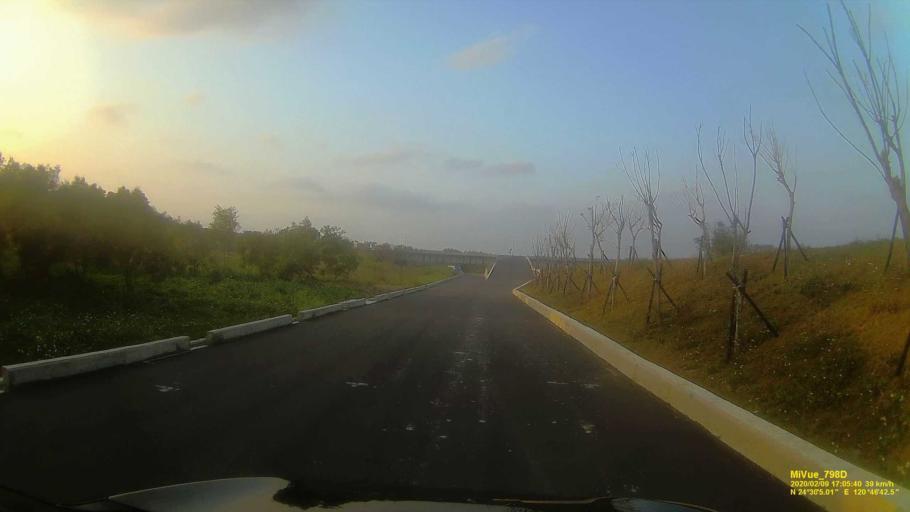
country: TW
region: Taiwan
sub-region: Miaoli
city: Miaoli
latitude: 24.5015
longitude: 120.7784
